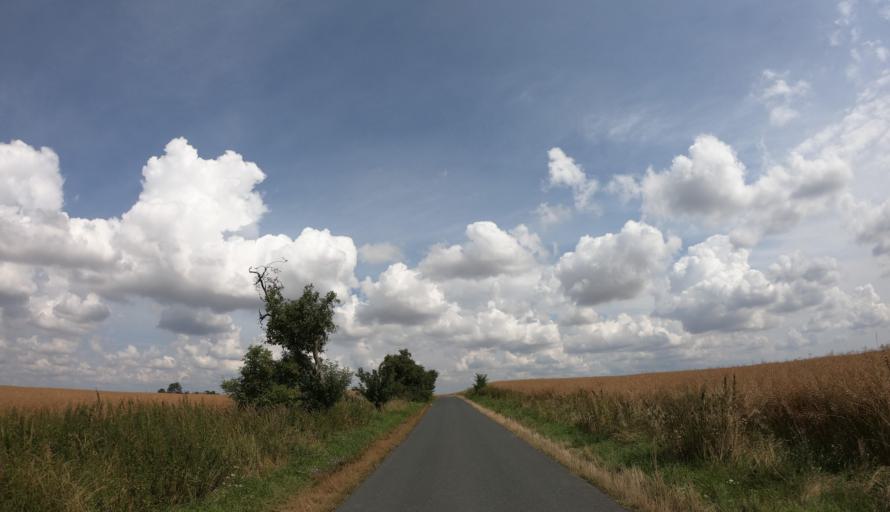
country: PL
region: West Pomeranian Voivodeship
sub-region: Powiat pyrzycki
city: Lipiany
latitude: 53.0473
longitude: 14.8941
